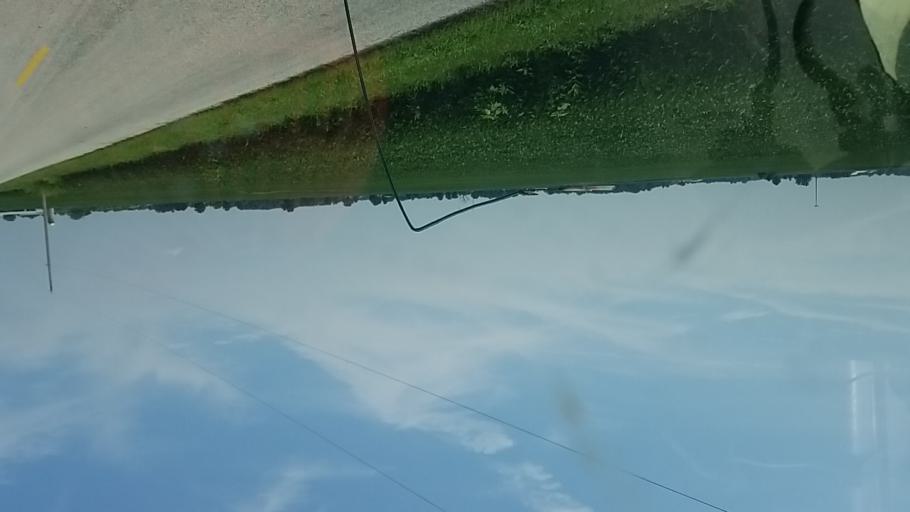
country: US
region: Ohio
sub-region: Marion County
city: Marion
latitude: 40.5972
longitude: -83.0489
